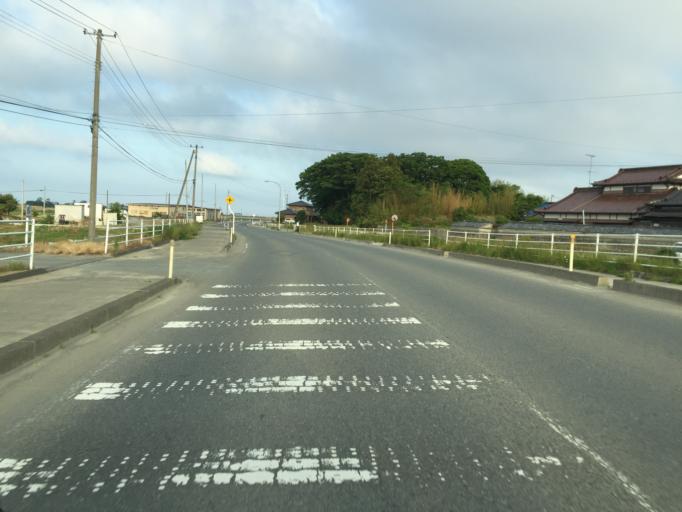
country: JP
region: Miyagi
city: Marumori
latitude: 37.7830
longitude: 140.9641
